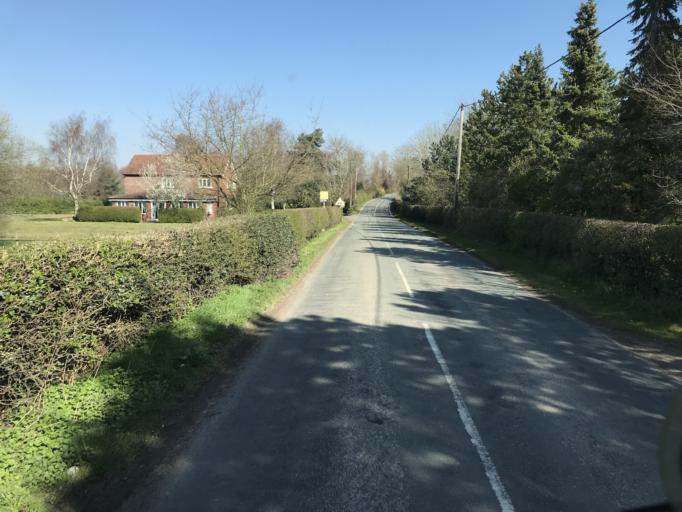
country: GB
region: England
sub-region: Cheshire West and Chester
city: Waverton
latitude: 53.1640
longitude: -2.8254
